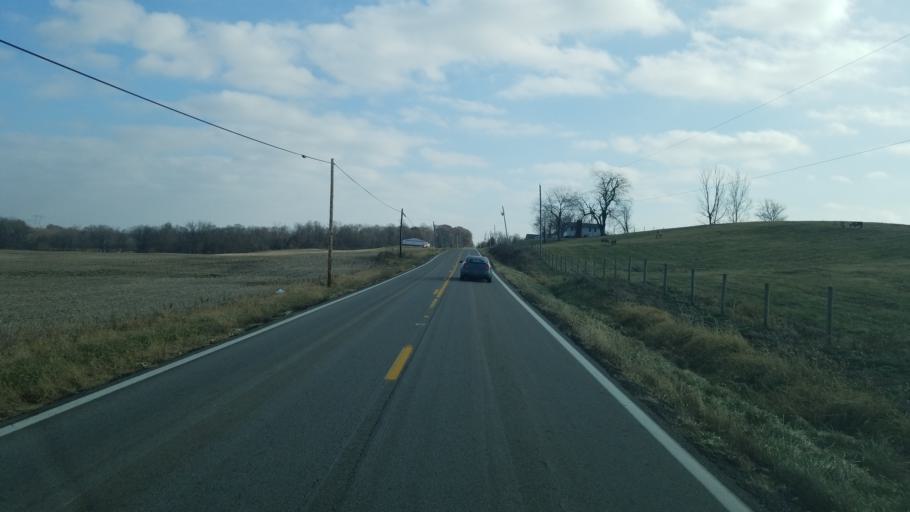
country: US
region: Ohio
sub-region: Licking County
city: Utica
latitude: 40.1741
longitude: -82.4970
